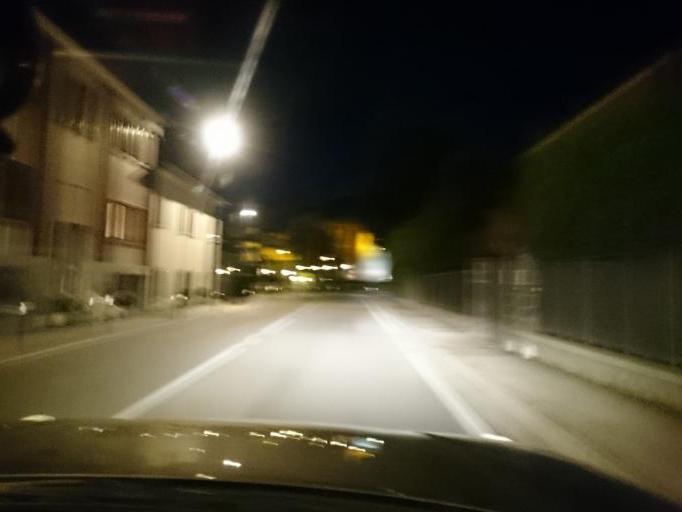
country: IT
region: Veneto
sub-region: Provincia di Padova
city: Este
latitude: 45.2307
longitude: 11.6612
